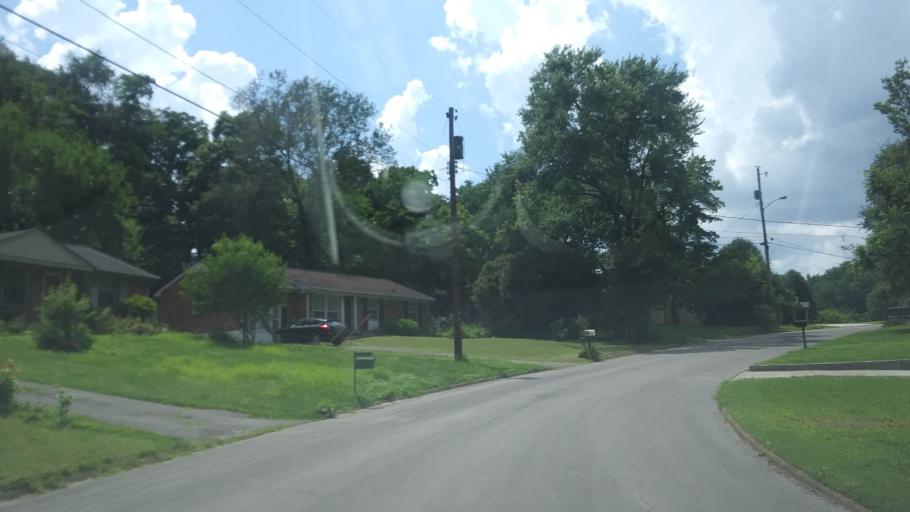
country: US
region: Tennessee
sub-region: Davidson County
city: Oak Hill
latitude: 36.0756
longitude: -86.7051
